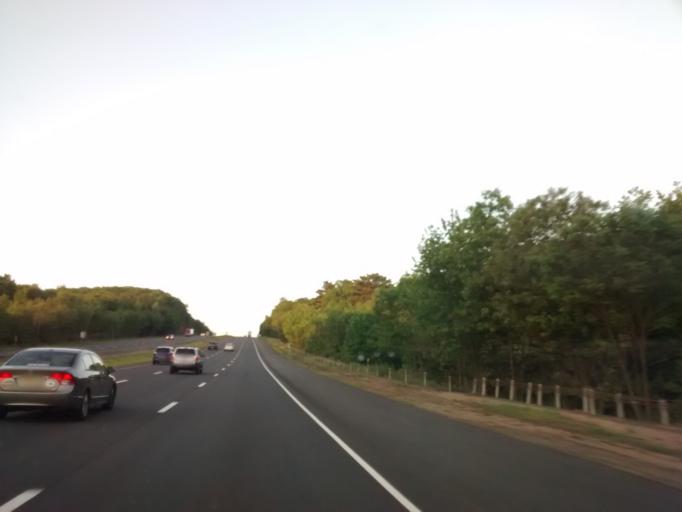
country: US
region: Connecticut
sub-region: Tolland County
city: Stafford
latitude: 41.9399
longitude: -72.2253
